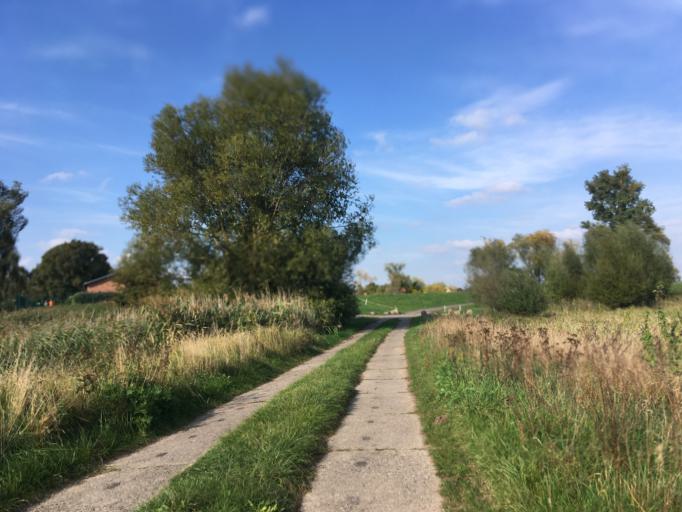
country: DE
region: Brandenburg
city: Schwedt (Oder)
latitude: 53.0459
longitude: 14.2771
